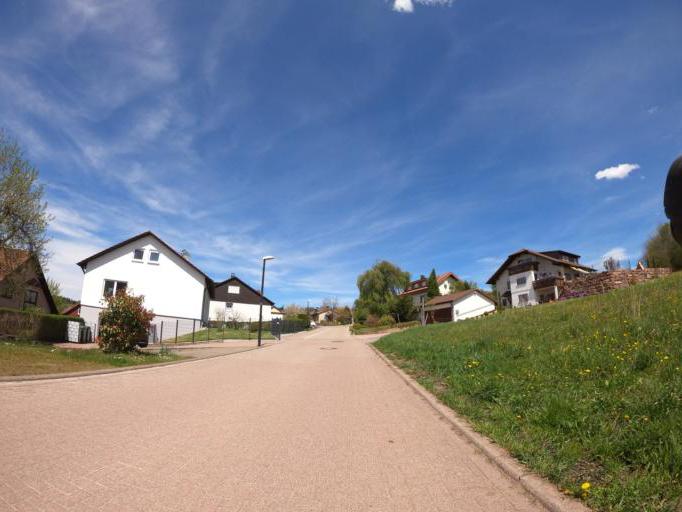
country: DE
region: Baden-Wuerttemberg
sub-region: Karlsruhe Region
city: Engelsbrand
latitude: 48.8333
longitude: 8.6455
